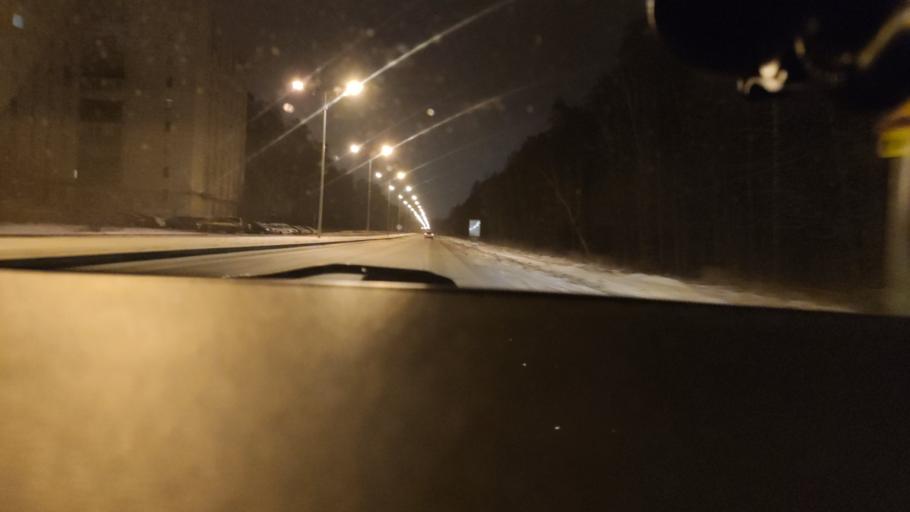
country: RU
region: Perm
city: Kultayevo
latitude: 58.0159
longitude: 55.9823
